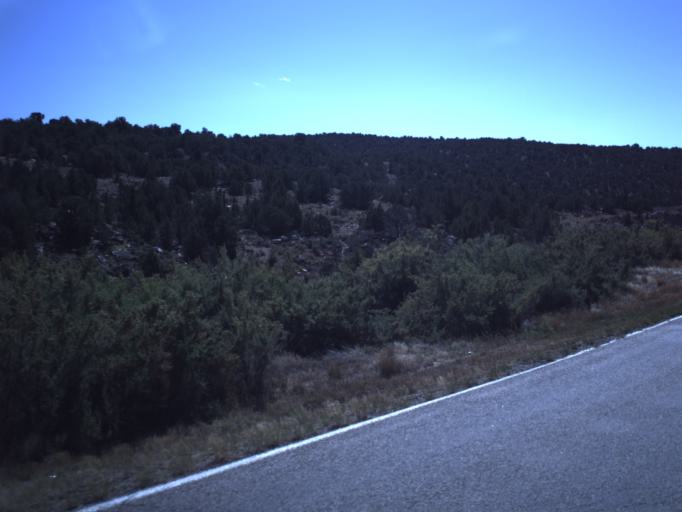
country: US
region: Utah
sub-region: Grand County
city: Moab
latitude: 38.3139
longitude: -109.3529
